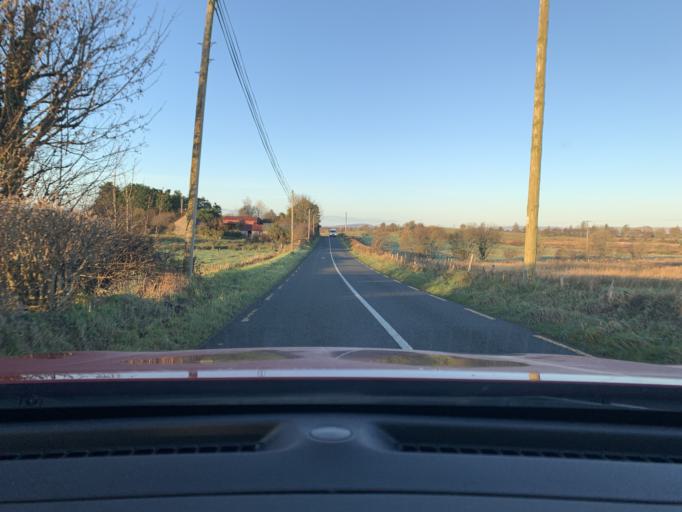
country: IE
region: Connaught
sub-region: Sligo
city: Ballymote
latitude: 54.0862
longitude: -8.5381
